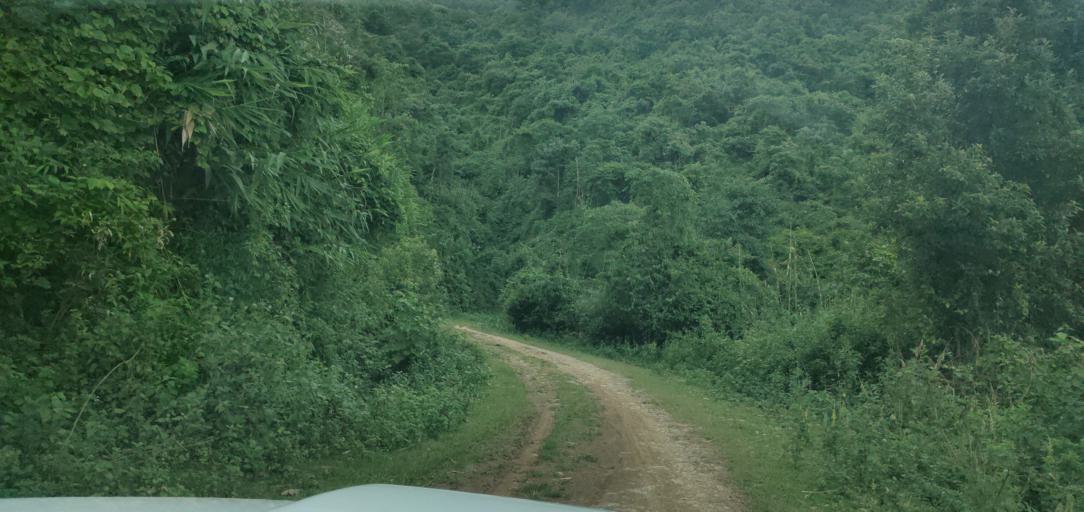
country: LA
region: Phongsali
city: Phongsali
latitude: 21.4407
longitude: 102.3250
